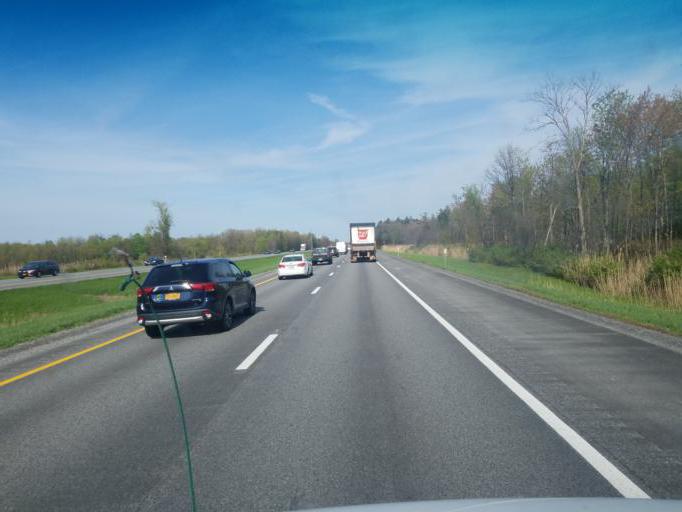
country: US
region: New York
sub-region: Madison County
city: Bolivar
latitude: 43.0921
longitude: -75.8992
